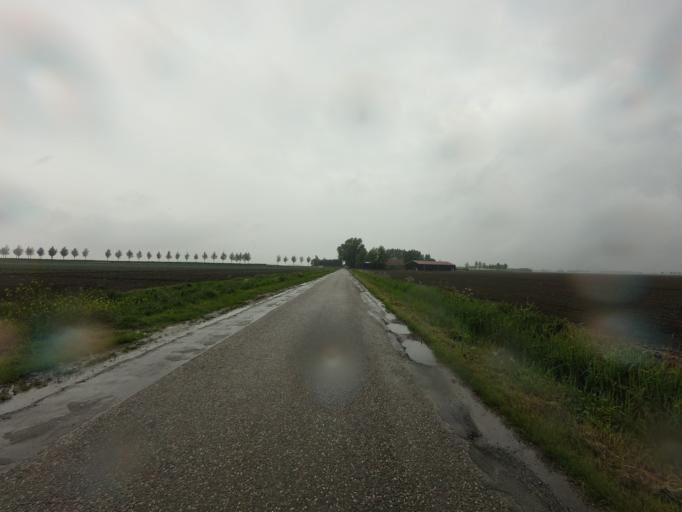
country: NL
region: South Holland
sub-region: Gemeente Goeree-Overflakkee
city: Dirksland
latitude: 51.7227
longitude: 4.1144
